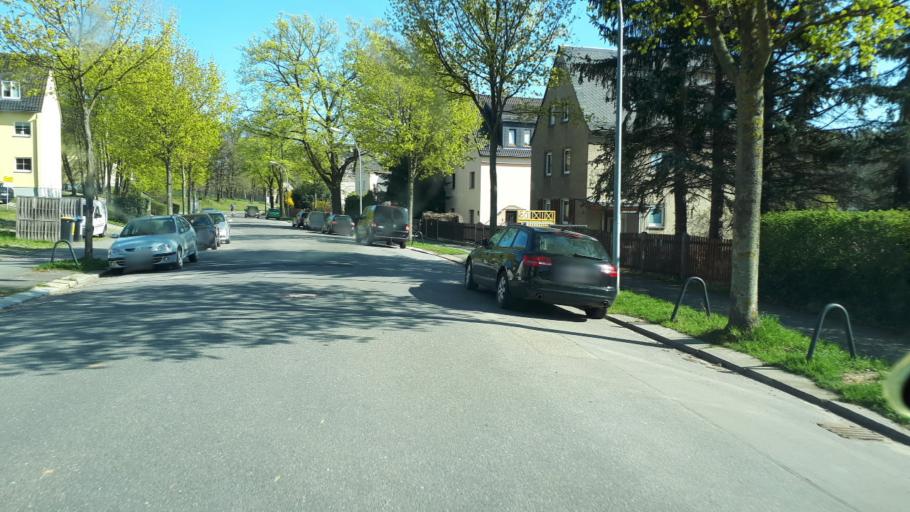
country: DE
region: Saxony
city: Chemnitz
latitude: 50.7960
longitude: 12.9359
